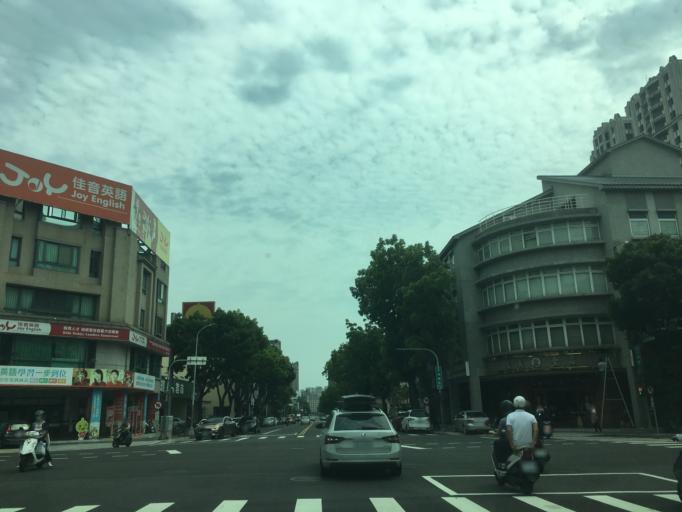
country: TW
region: Taiwan
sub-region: Taichung City
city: Taichung
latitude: 24.1352
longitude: 120.6500
